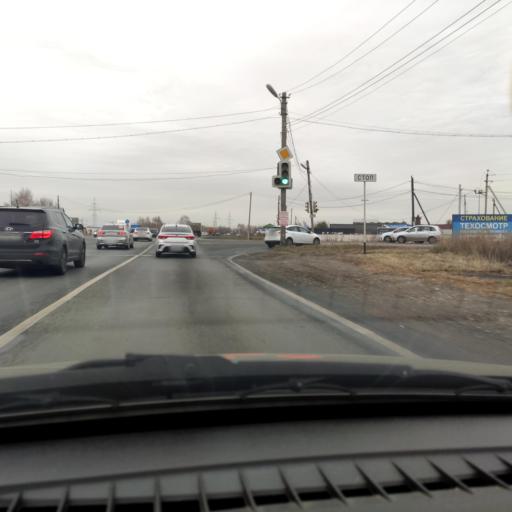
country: RU
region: Samara
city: Tol'yatti
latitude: 53.5780
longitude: 49.4020
